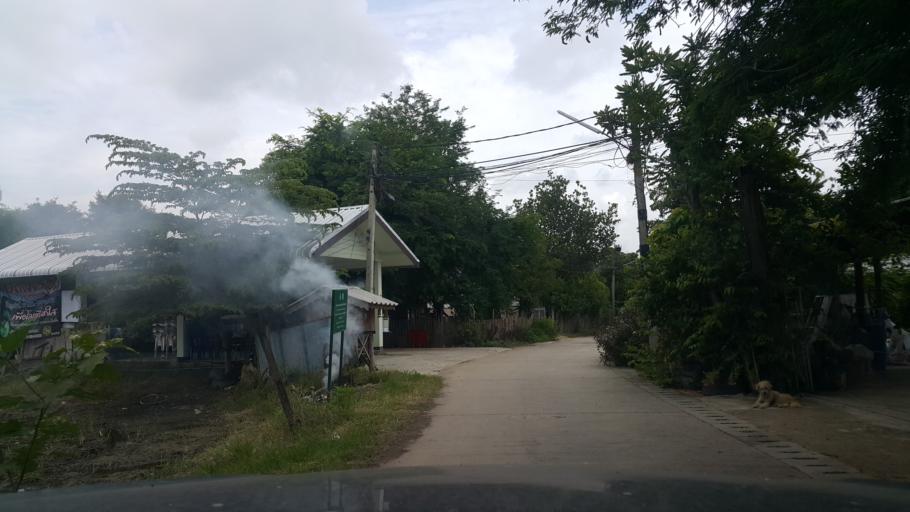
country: TH
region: Lamphun
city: Ban Thi
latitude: 18.6704
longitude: 99.1504
